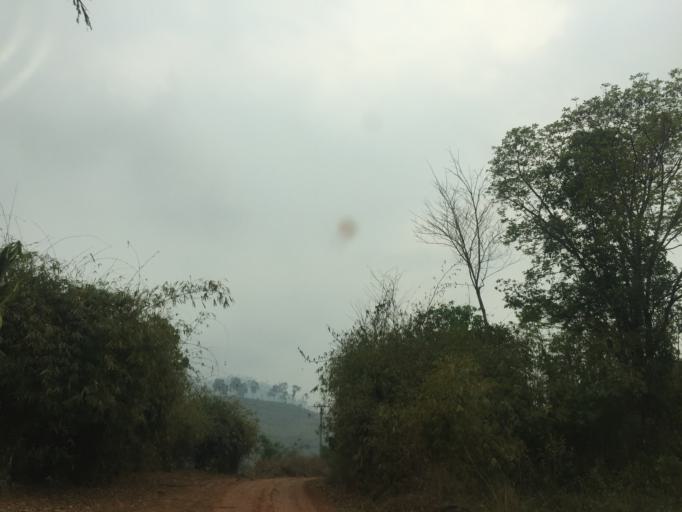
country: TH
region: Nan
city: Bo Kluea
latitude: 18.8555
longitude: 101.4236
